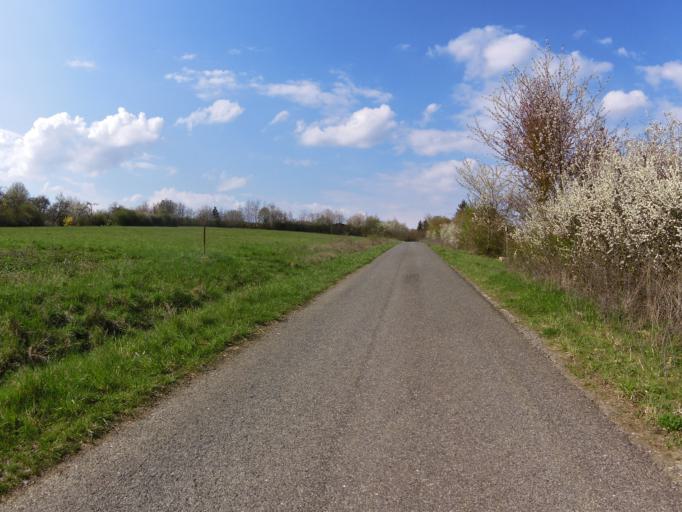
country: DE
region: Bavaria
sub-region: Regierungsbezirk Unterfranken
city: Rimpar
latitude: 49.8662
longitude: 9.9647
